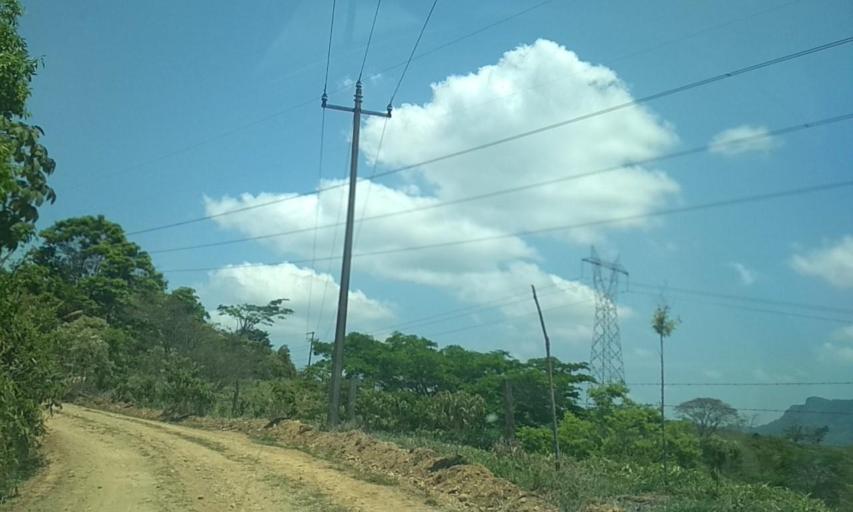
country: MX
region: Chiapas
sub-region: Tecpatan
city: Raudales Malpaso
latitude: 17.3972
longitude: -93.7459
